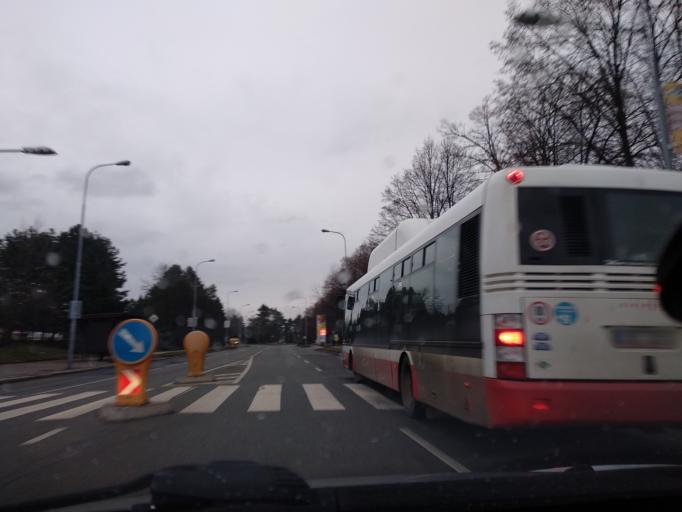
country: CZ
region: South Moravian
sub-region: Mesto Brno
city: Brno
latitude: 49.2226
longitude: 16.6252
